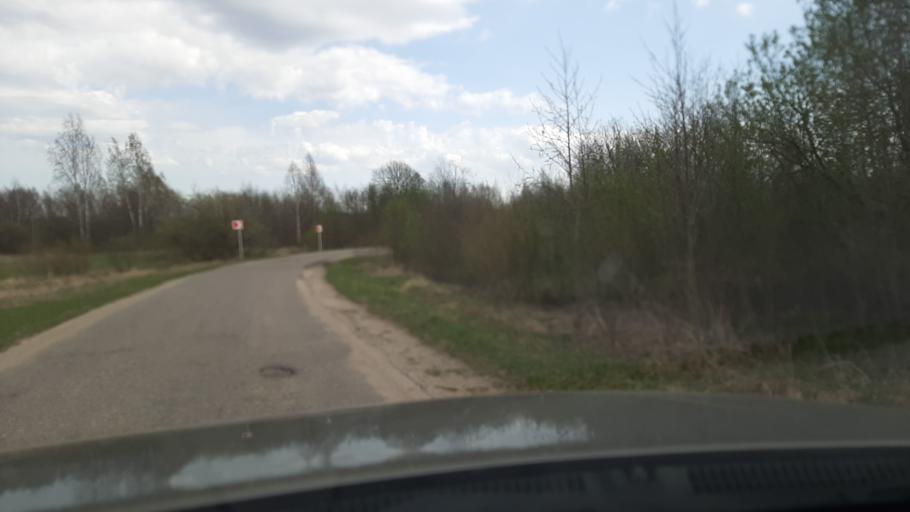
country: RU
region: Ivanovo
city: Furmanov
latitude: 57.3019
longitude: 41.1650
